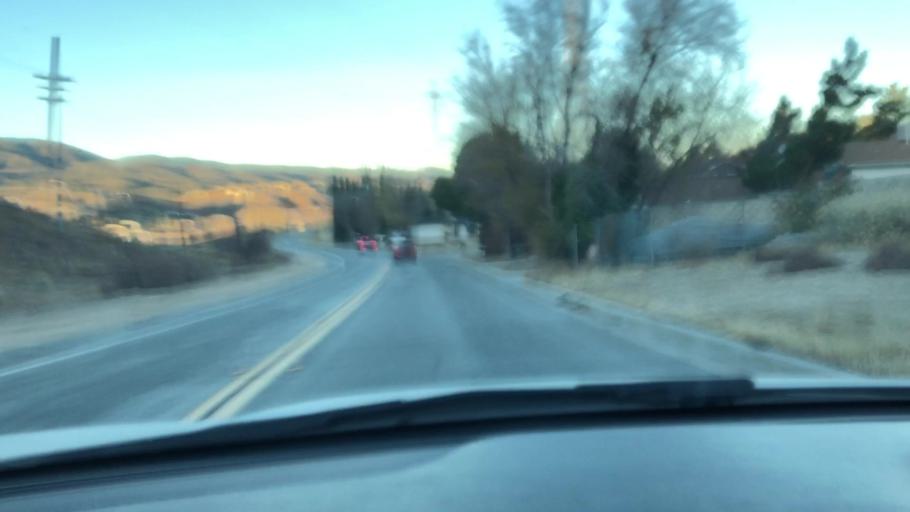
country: US
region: California
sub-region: Los Angeles County
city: Green Valley
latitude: 34.6601
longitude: -118.3670
